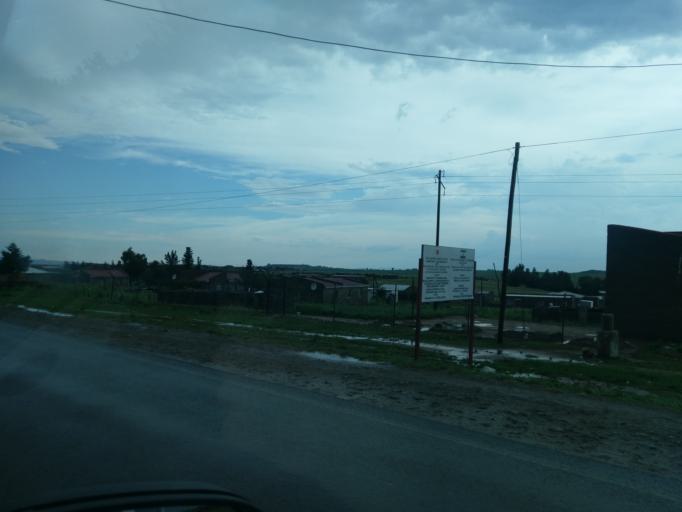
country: LS
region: Mafeteng
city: Mafeteng
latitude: -29.7989
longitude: 27.2114
